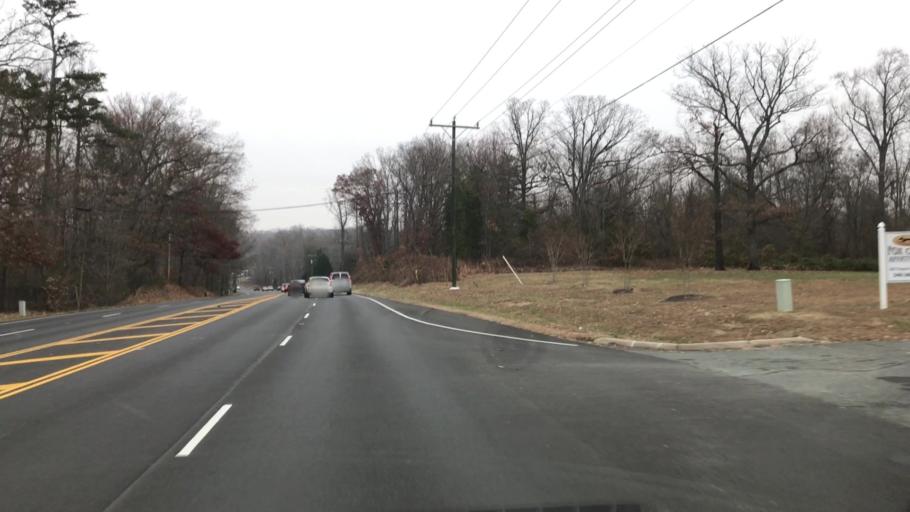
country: US
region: Virginia
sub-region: Stafford County
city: Falmouth
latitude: 38.3462
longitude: -77.4582
